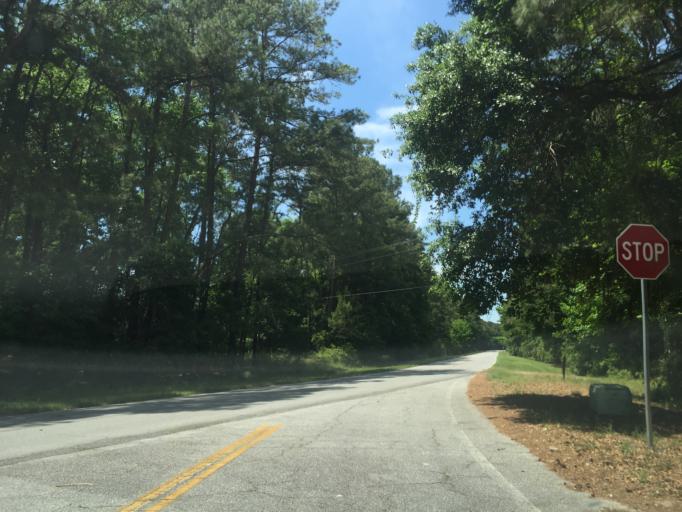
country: US
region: Georgia
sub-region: Chatham County
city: Skidaway Island
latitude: 31.9610
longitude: -81.0292
